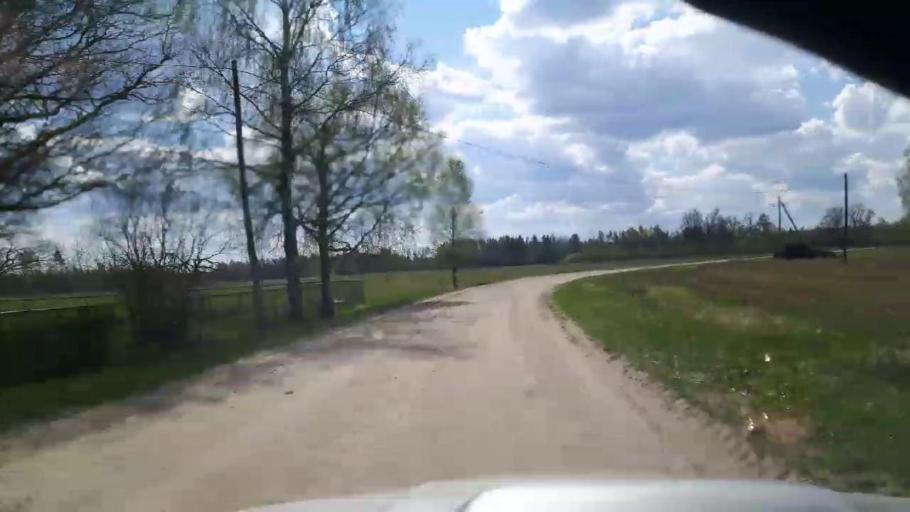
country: EE
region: Paernumaa
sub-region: Tootsi vald
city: Tootsi
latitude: 58.4721
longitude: 24.9012
